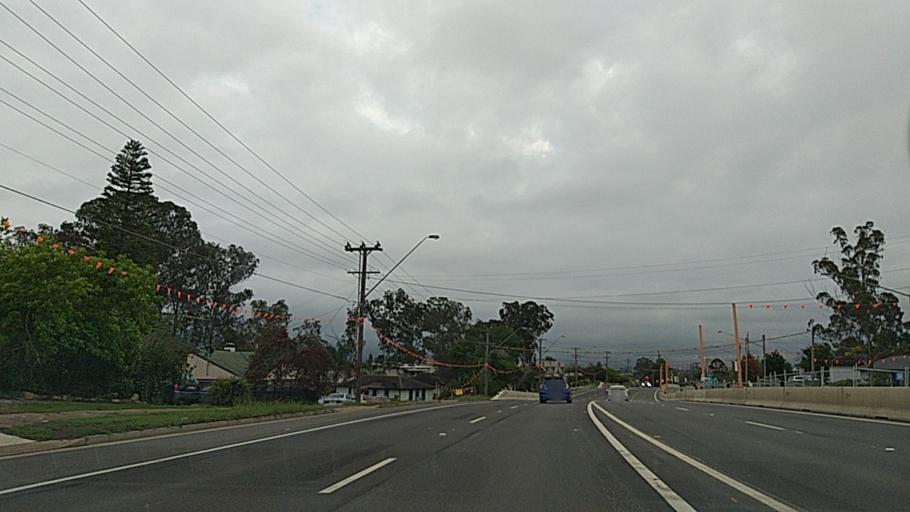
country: AU
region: New South Wales
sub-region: Penrith Municipality
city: Kingswood Park
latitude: -33.7664
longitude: 150.7100
